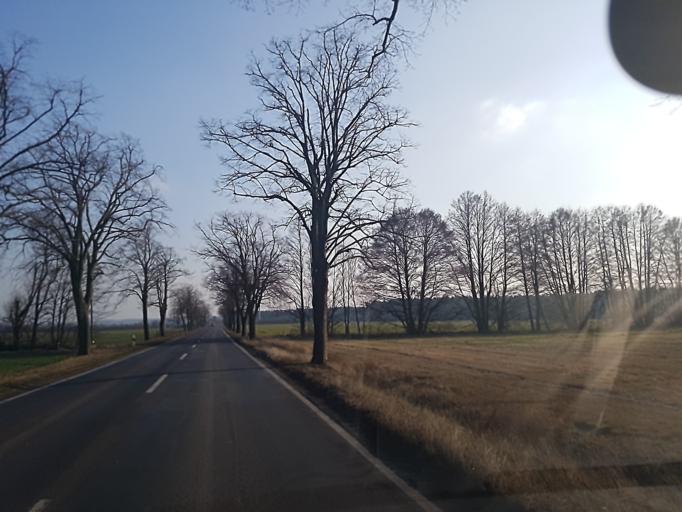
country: DE
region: Brandenburg
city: Wenzlow
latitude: 52.2966
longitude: 12.4569
